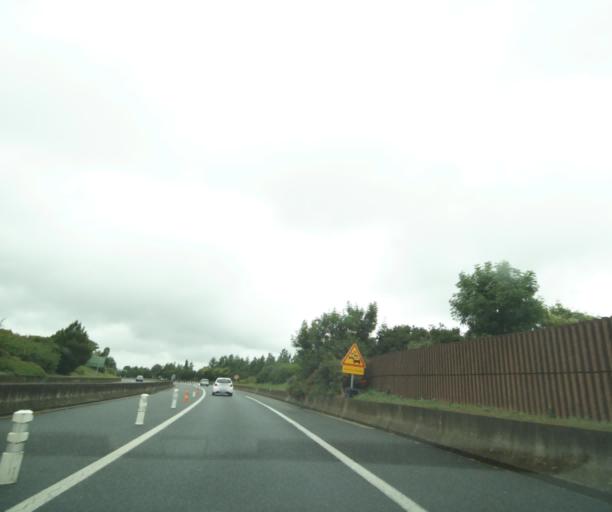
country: FR
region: Midi-Pyrenees
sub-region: Departement de l'Aveyron
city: Olemps
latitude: 44.3276
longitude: 2.5580
